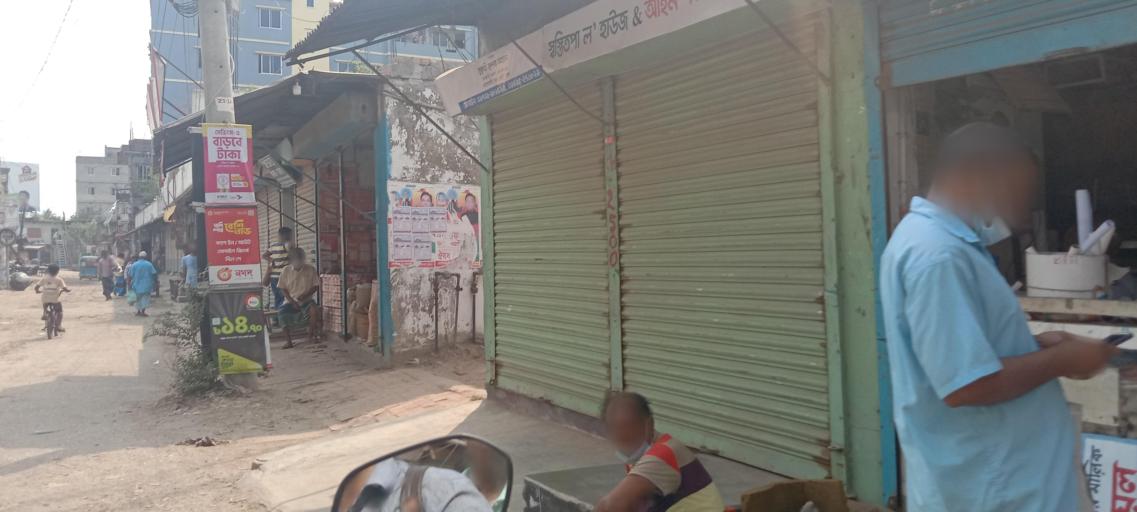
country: BD
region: Dhaka
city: Azimpur
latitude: 23.7132
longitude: 90.3581
